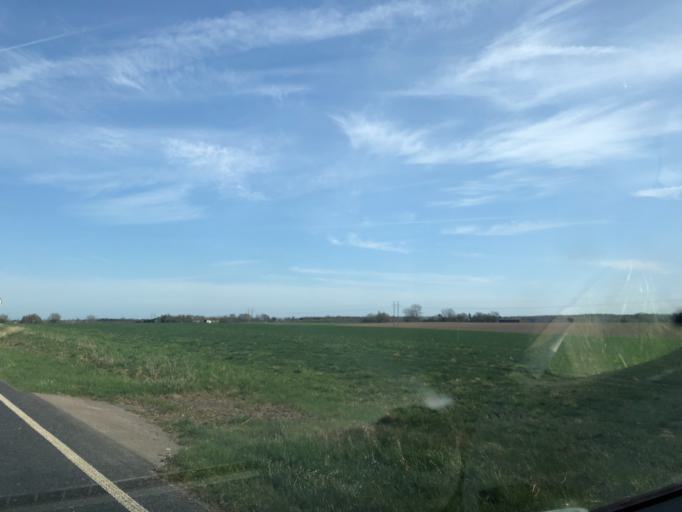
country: DK
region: Zealand
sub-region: Faxe Kommune
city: Fakse Ladeplads
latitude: 55.2799
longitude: 12.2047
